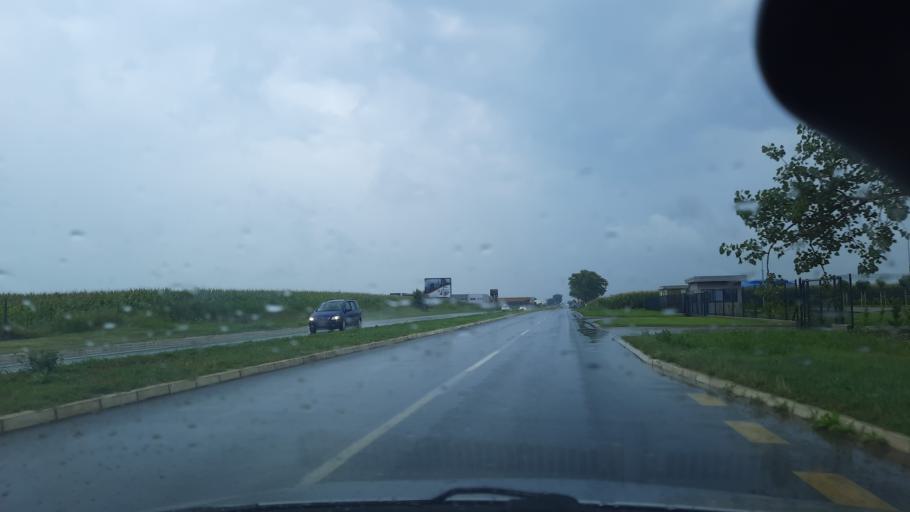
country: RS
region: Autonomna Pokrajina Vojvodina
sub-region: Sremski Okrug
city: Stara Pazova
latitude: 44.9864
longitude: 20.1886
